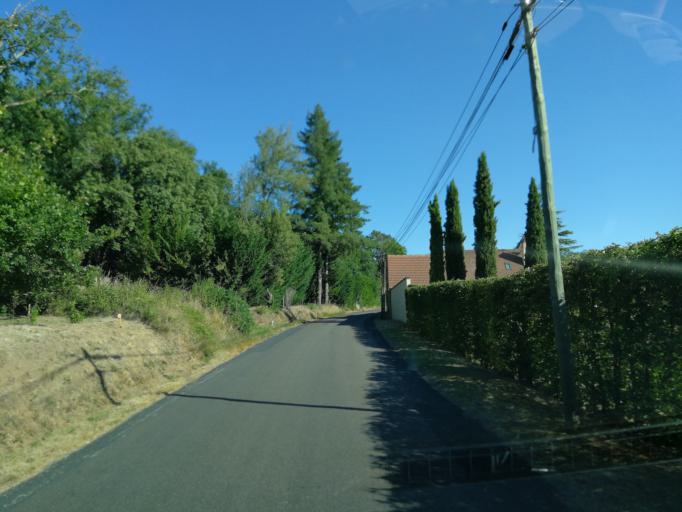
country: FR
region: Midi-Pyrenees
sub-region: Departement du Lot
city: Gourdon
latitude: 44.7747
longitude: 1.3669
